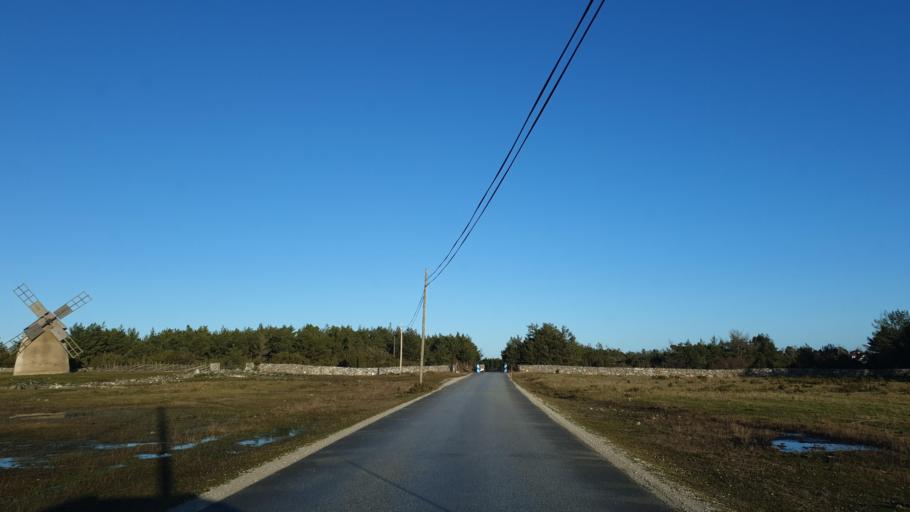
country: SE
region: Gotland
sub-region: Gotland
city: Slite
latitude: 57.9494
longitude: 19.1568
